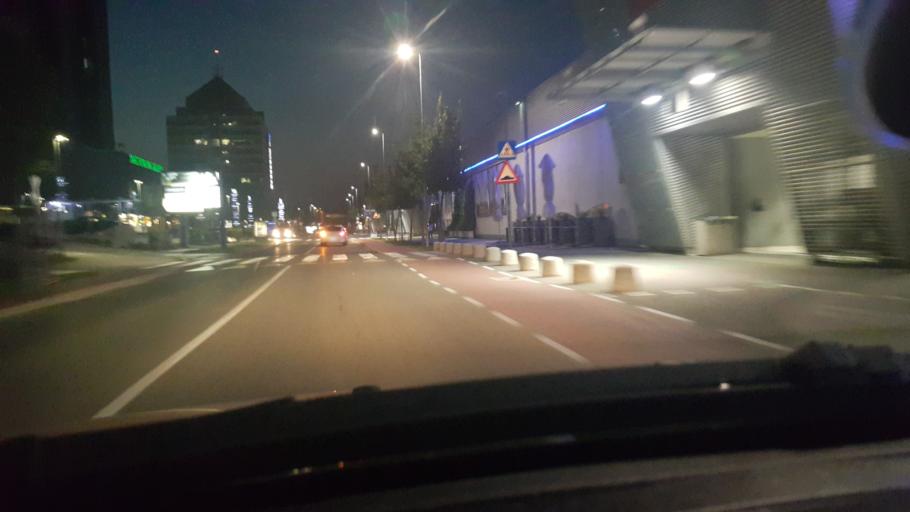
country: SI
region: Ljubljana
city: Ljubljana
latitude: 46.0659
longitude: 14.5426
